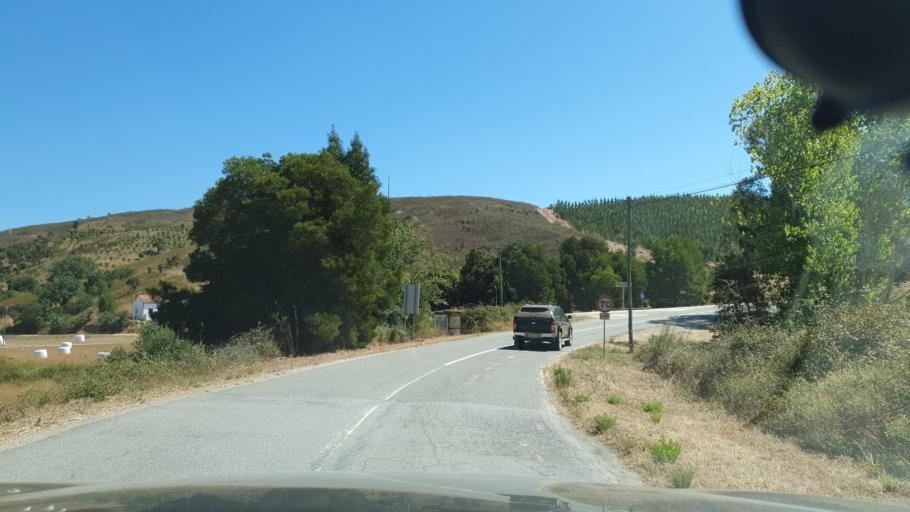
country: PT
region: Faro
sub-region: Monchique
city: Monchique
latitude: 37.4327
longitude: -8.5304
